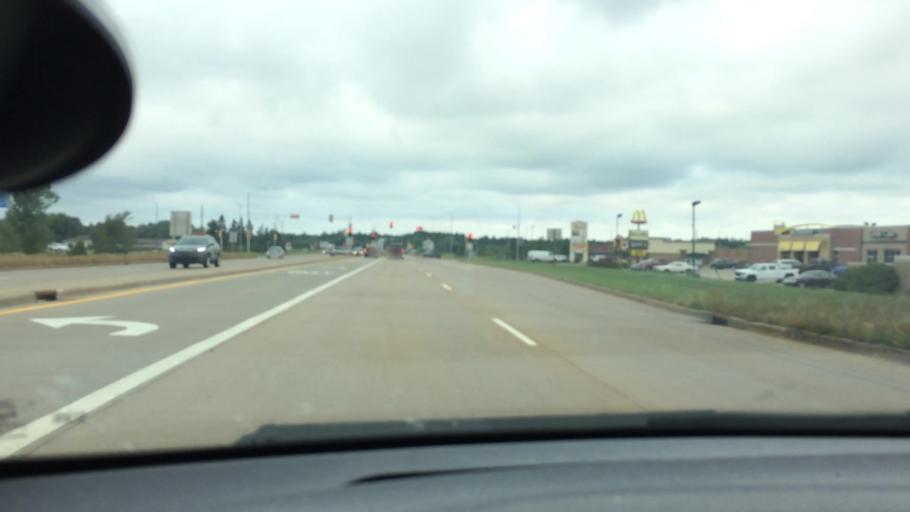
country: US
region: Wisconsin
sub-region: Chippewa County
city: Lake Hallie
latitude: 44.8844
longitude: -91.4178
